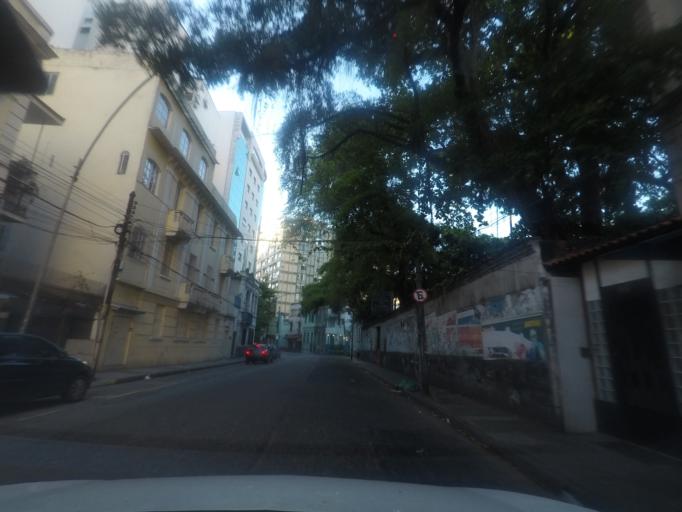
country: BR
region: Rio de Janeiro
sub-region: Rio De Janeiro
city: Rio de Janeiro
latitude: -22.9293
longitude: -43.1794
